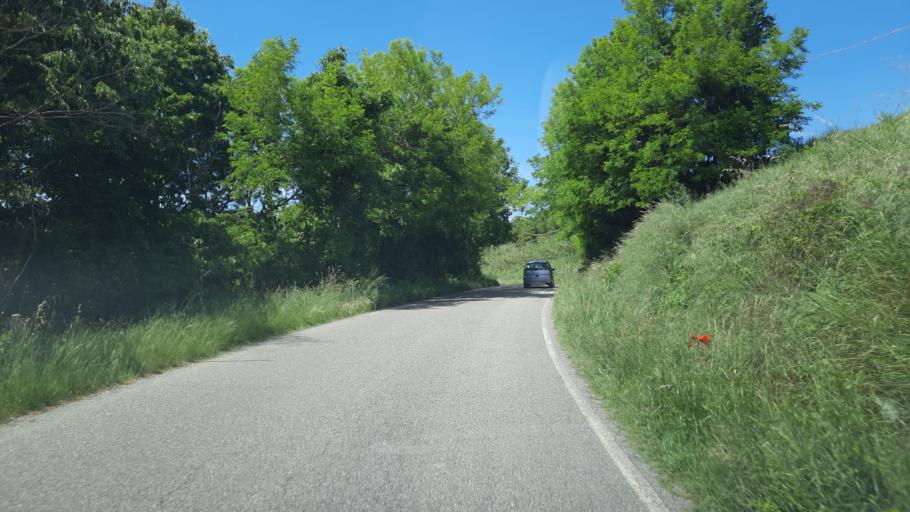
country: IT
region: Piedmont
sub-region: Provincia di Alessandria
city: Alfiano Natta
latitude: 45.0479
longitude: 8.2175
